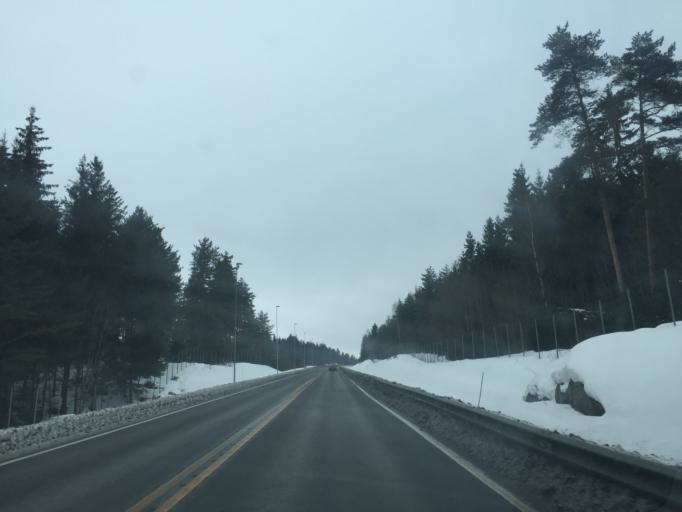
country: NO
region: Hedmark
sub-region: Loten
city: Loten
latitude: 60.7452
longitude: 11.3003
